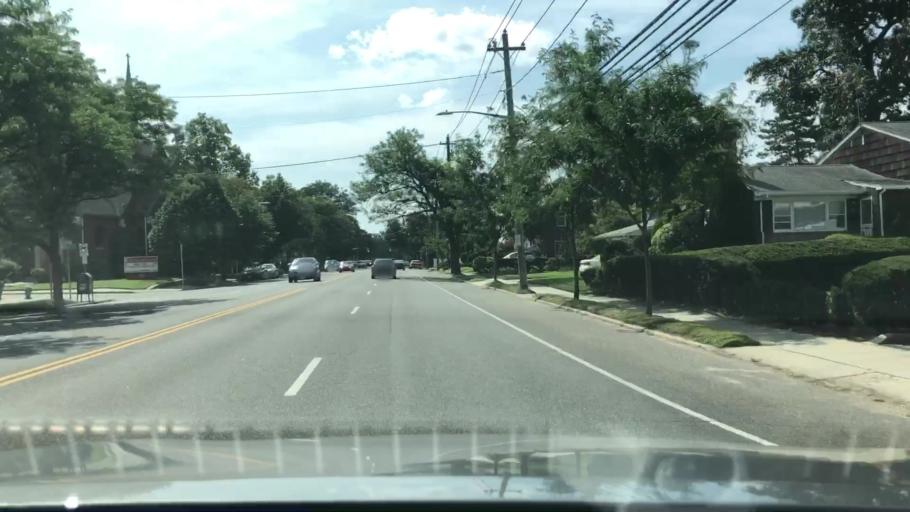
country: US
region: New York
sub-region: Nassau County
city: South Hempstead
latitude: 40.6773
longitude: -73.6140
